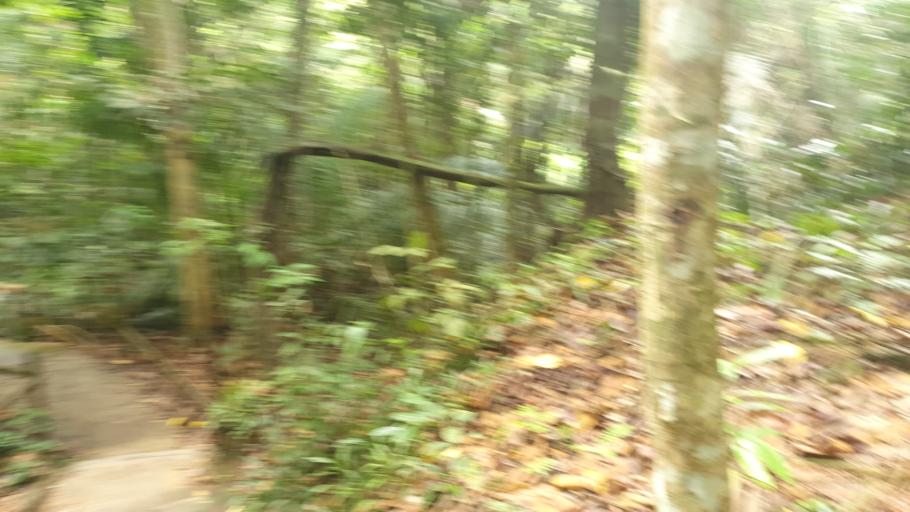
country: SG
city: Singapore
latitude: 1.3602
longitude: 103.8221
